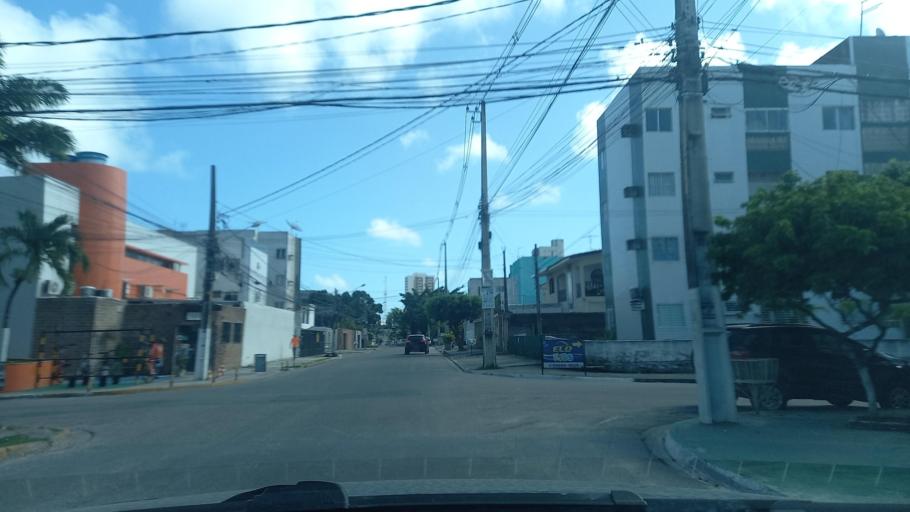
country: BR
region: Pernambuco
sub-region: Jaboatao Dos Guararapes
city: Jaboatao
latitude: -8.1946
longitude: -34.9221
